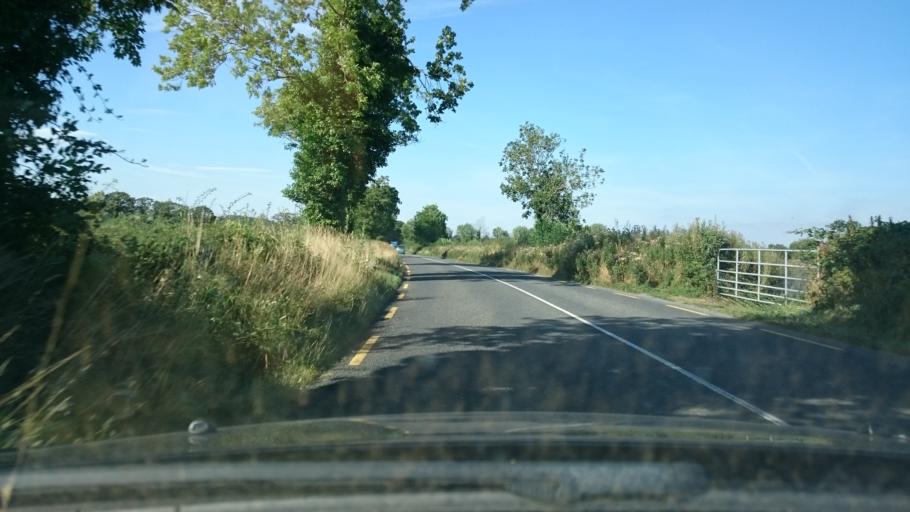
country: IE
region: Leinster
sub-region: Kilkenny
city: Graiguenamanagh
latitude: 52.5618
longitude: -6.9522
